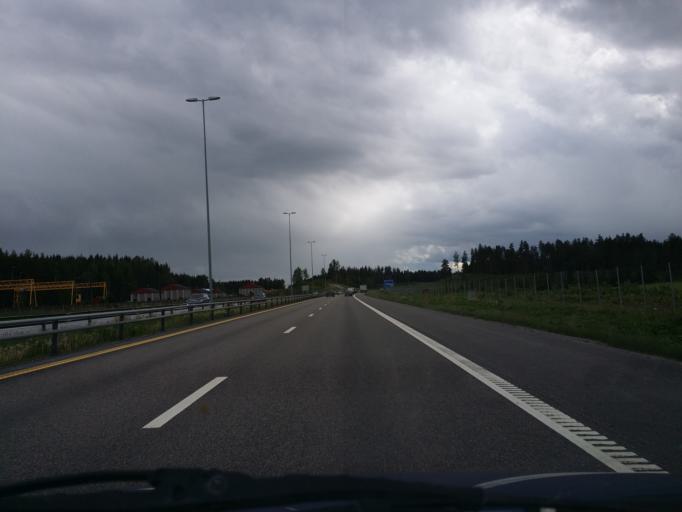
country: NO
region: Akershus
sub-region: Ullensaker
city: Jessheim
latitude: 60.1981
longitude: 11.1895
